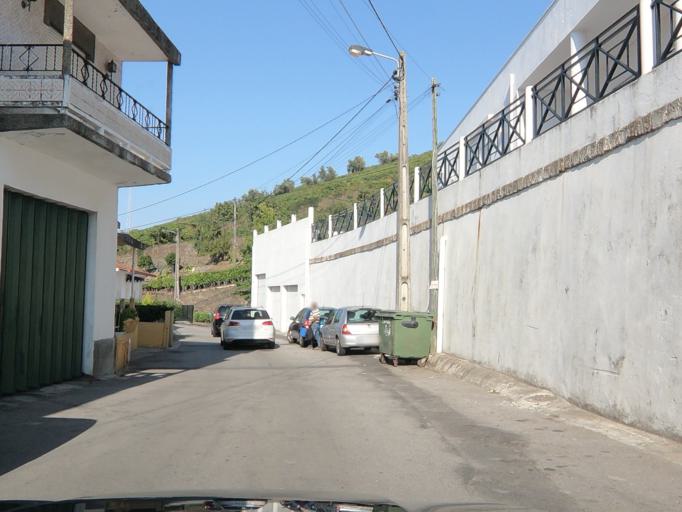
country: PT
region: Vila Real
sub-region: Peso da Regua
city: Peso da Regua
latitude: 41.1877
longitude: -7.7749
